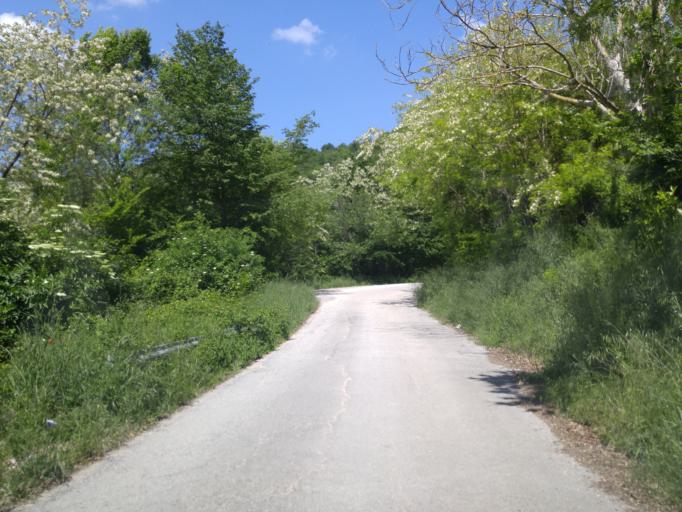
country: IT
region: The Marches
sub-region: Provincia di Pesaro e Urbino
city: Fermignano
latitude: 43.7125
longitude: 12.6759
